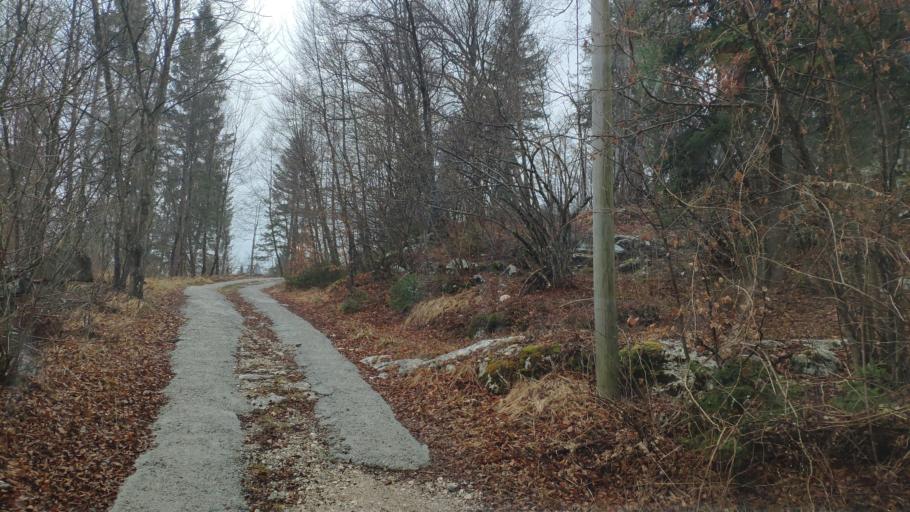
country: IT
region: Veneto
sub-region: Provincia di Vicenza
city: Rotzo
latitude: 45.8224
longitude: 11.3995
